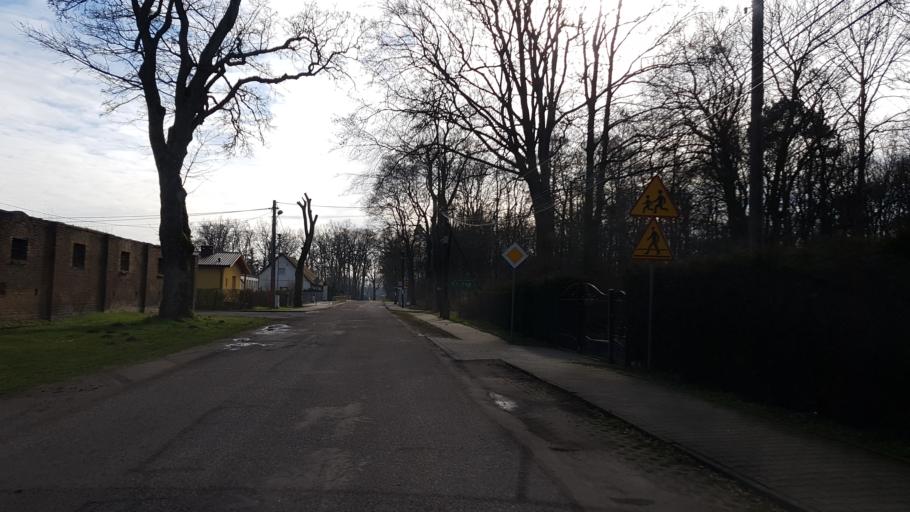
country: PL
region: West Pomeranian Voivodeship
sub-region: Powiat policki
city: Dobra
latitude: 53.5330
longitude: 14.3341
